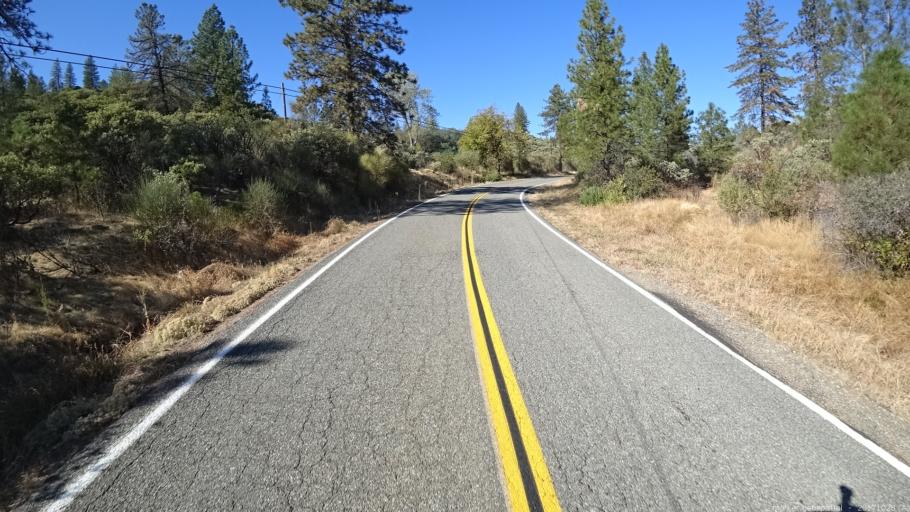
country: US
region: California
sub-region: Shasta County
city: Shasta
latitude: 40.6494
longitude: -122.4607
